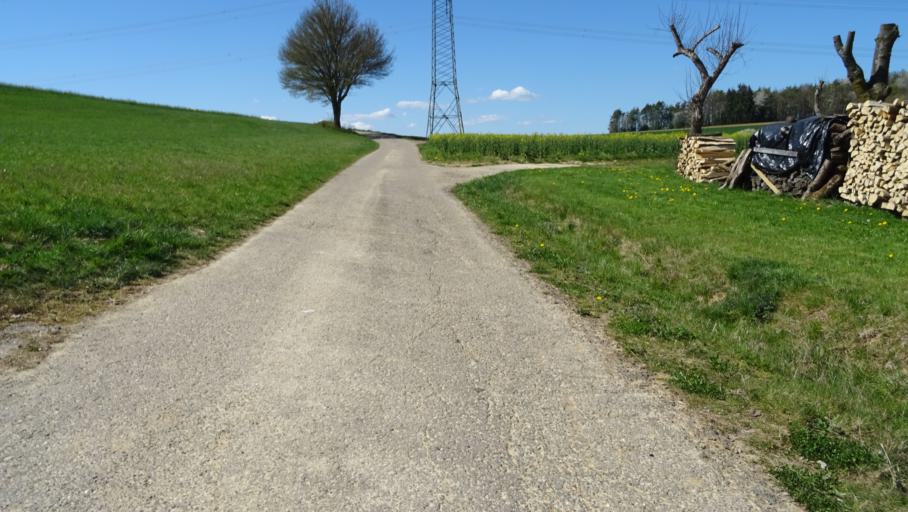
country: DE
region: Baden-Wuerttemberg
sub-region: Karlsruhe Region
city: Billigheim
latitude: 49.3945
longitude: 9.2491
